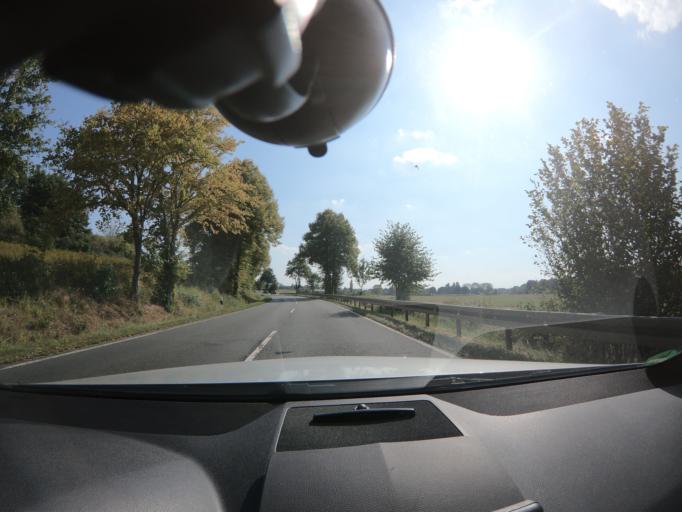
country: DE
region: Hesse
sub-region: Regierungsbezirk Giessen
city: Kirchhain
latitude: 50.8390
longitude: 8.9218
